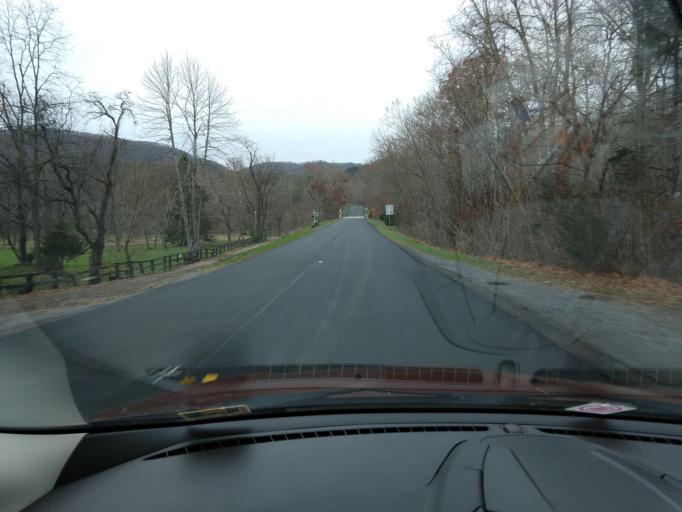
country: US
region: West Virginia
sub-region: Greenbrier County
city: White Sulphur Springs
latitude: 37.7333
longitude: -80.1907
